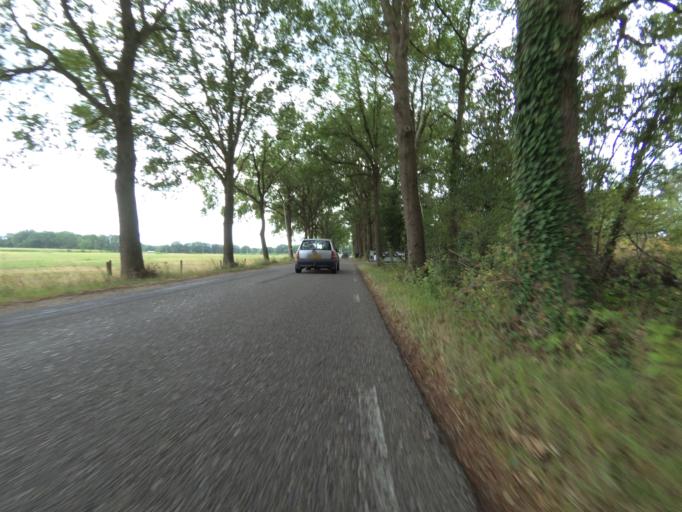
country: NL
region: Overijssel
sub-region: Gemeente Enschede
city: Enschede
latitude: 52.2601
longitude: 6.8950
